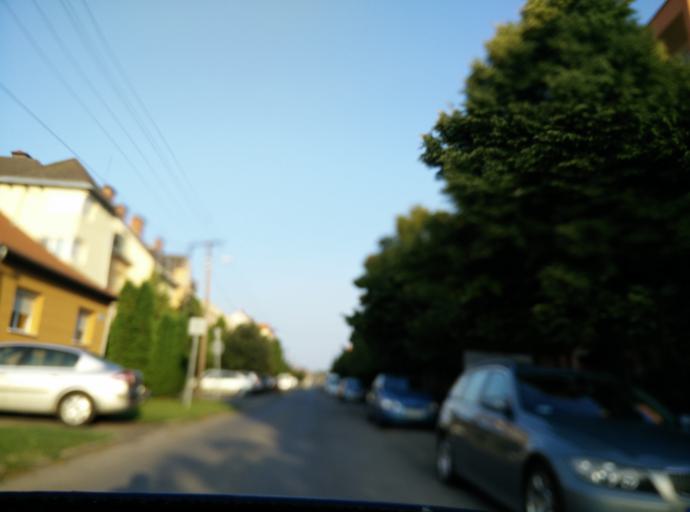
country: HU
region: Heves
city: Hatvan
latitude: 47.6645
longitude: 19.6910
